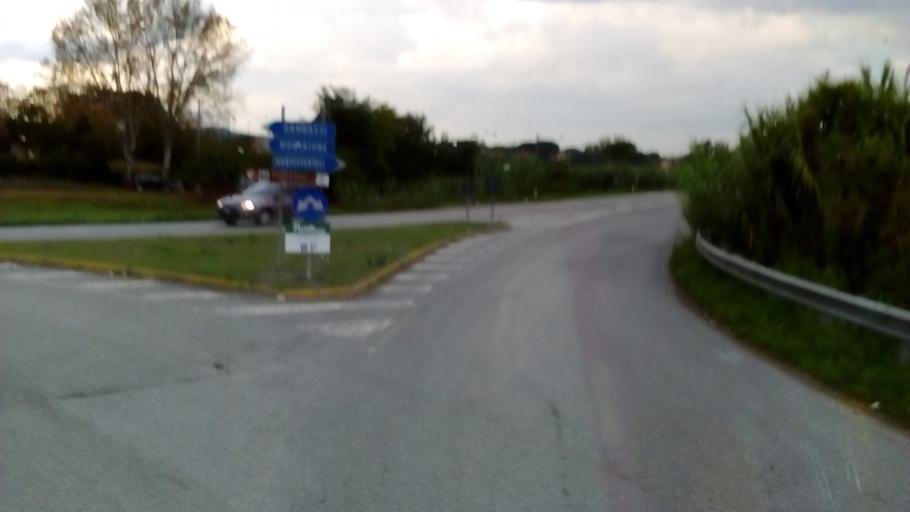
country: IT
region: Tuscany
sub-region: Province of Florence
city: Castelfiorentino
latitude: 43.5929
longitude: 10.9725
